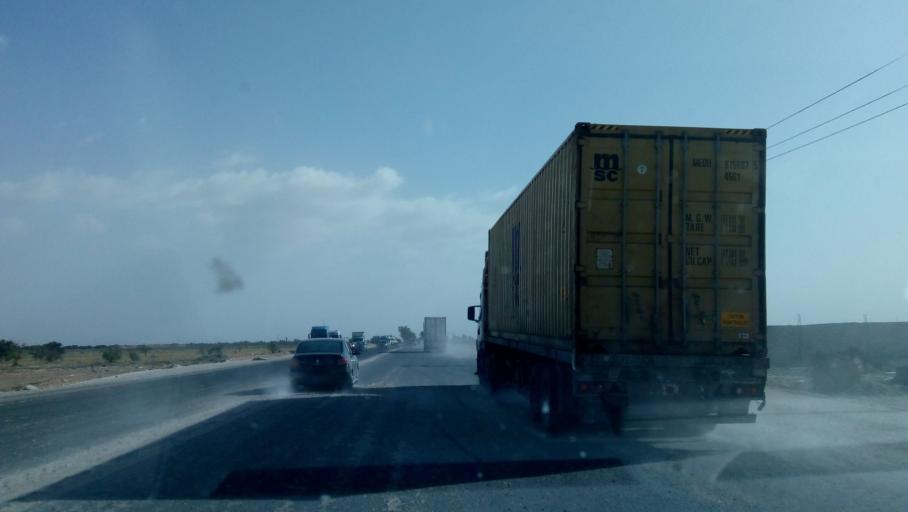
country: TN
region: Qabis
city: Gabes
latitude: 33.8838
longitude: 10.0118
